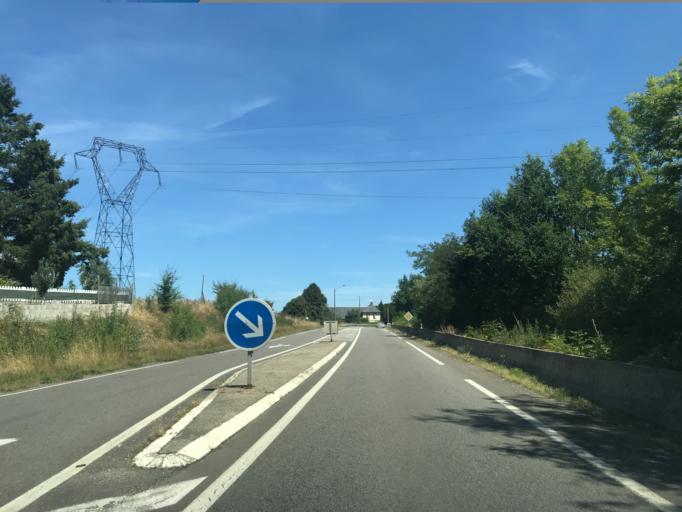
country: FR
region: Limousin
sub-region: Departement de la Correze
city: Naves
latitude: 45.3095
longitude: 1.8243
